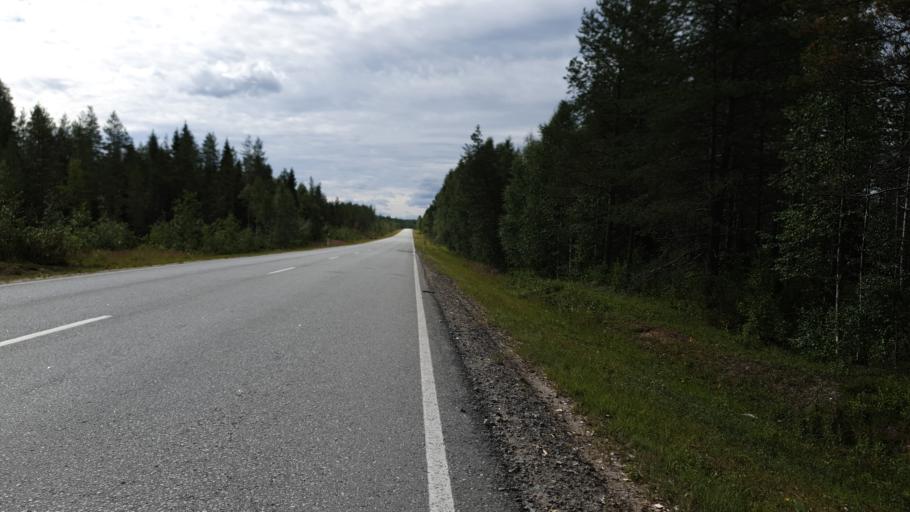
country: FI
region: Kainuu
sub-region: Kehys-Kainuu
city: Kuhmo
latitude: 64.5286
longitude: 29.9450
